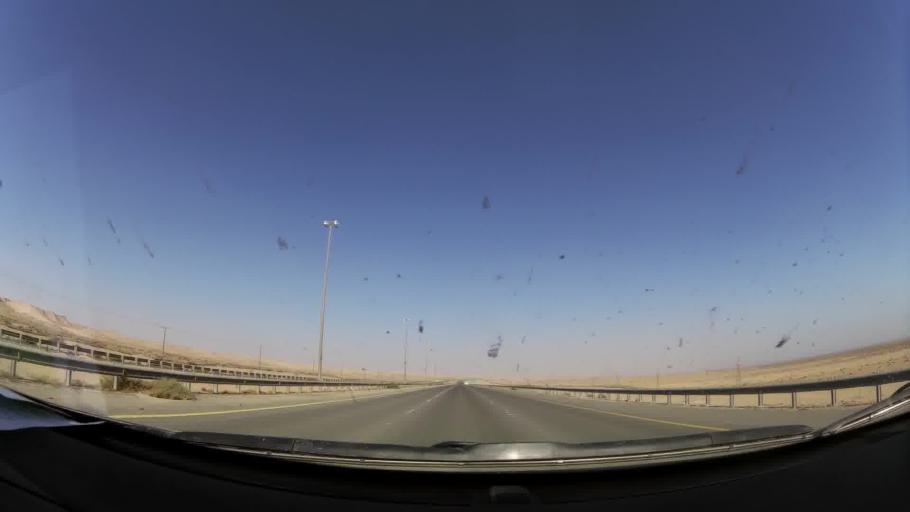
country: KW
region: Muhafazat al Jahra'
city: Al Jahra'
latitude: 29.4995
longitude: 47.7936
